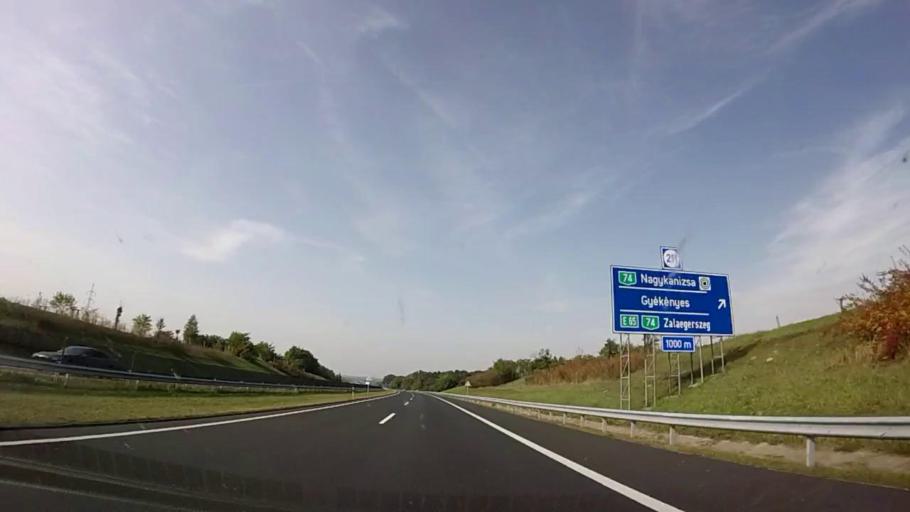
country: HU
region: Zala
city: Nagykanizsa
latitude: 46.4789
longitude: 16.9963
